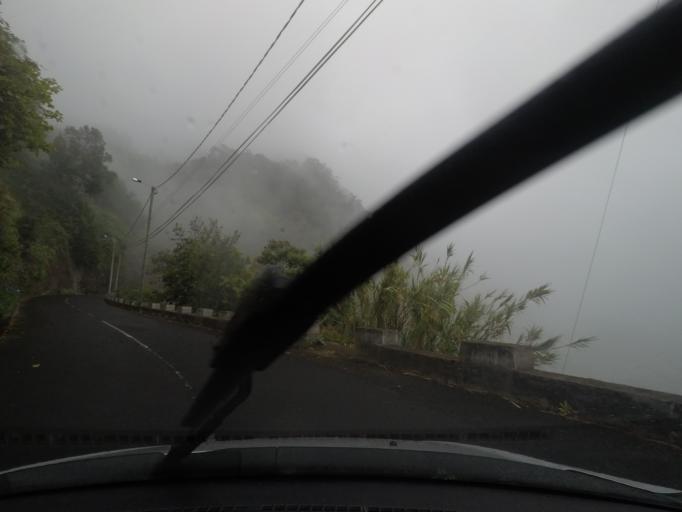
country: PT
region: Madeira
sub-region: Santana
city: Santana
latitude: 32.7773
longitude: -16.8634
